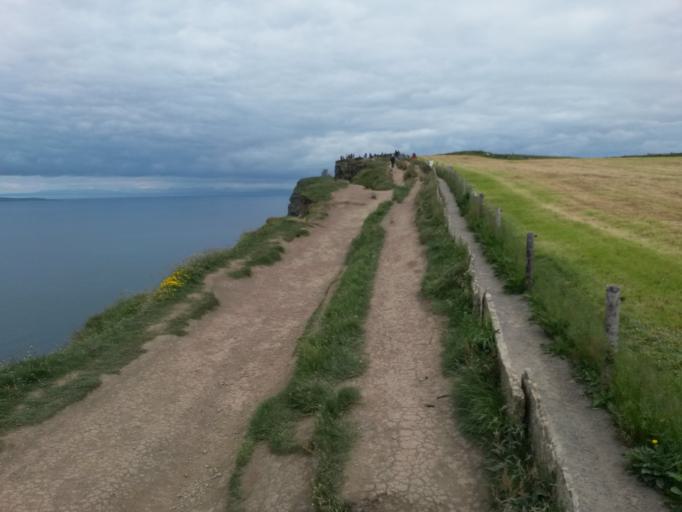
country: IE
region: Munster
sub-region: An Clar
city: Kilrush
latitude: 52.9664
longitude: -9.4313
